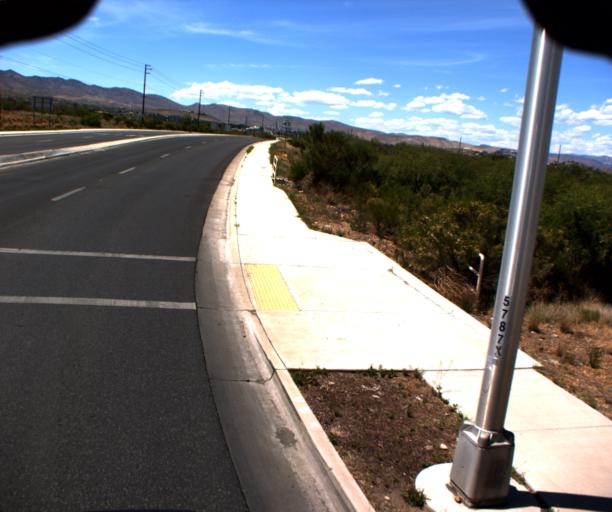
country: US
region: Arizona
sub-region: Yavapai County
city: Cottonwood
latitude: 34.7403
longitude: -112.0374
